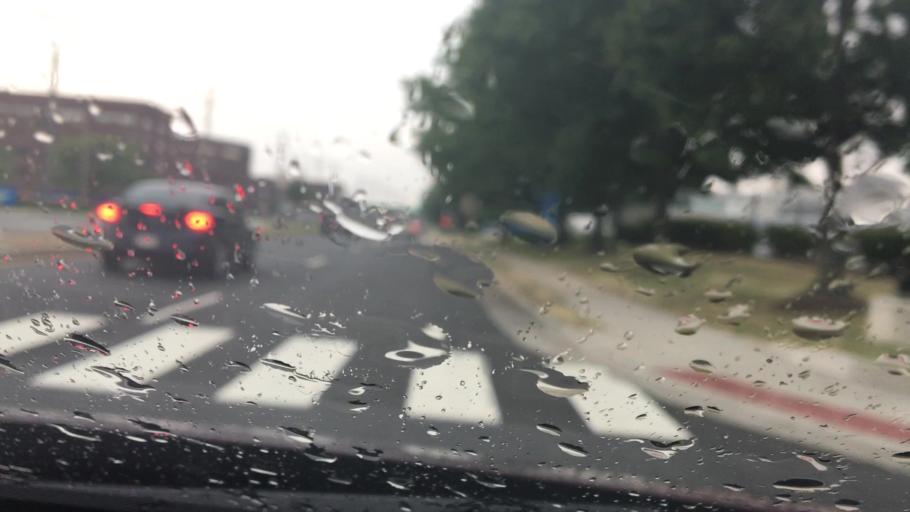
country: US
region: Virginia
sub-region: City of Fairfax
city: Fairfax
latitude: 38.8559
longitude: -77.3322
